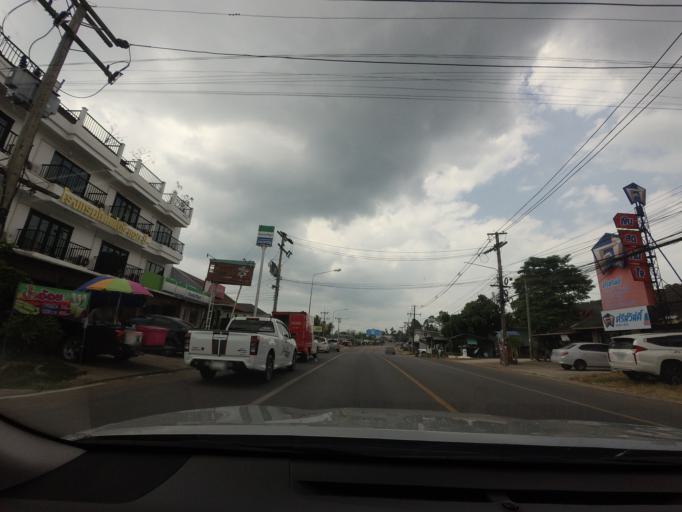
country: TH
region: Phangnga
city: Ban Ao Nang
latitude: 8.0527
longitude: 98.7608
